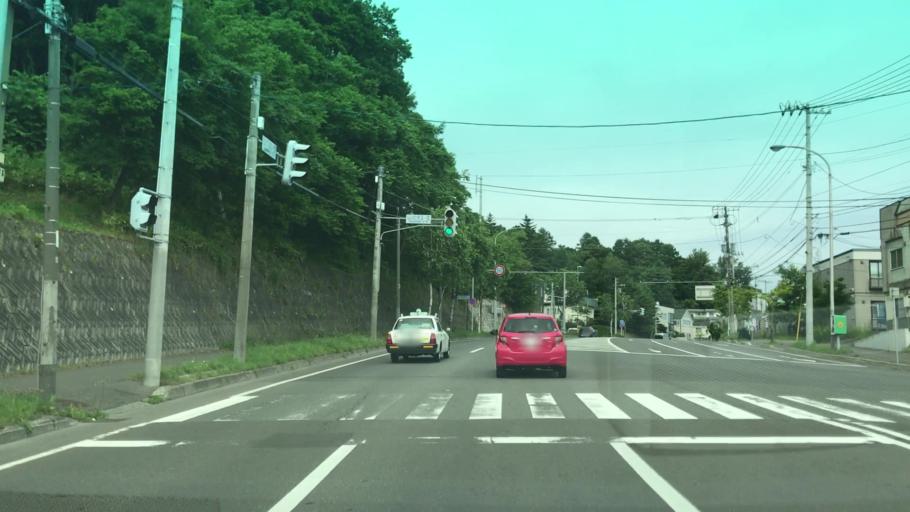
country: JP
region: Hokkaido
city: Sapporo
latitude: 43.0644
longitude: 141.2901
